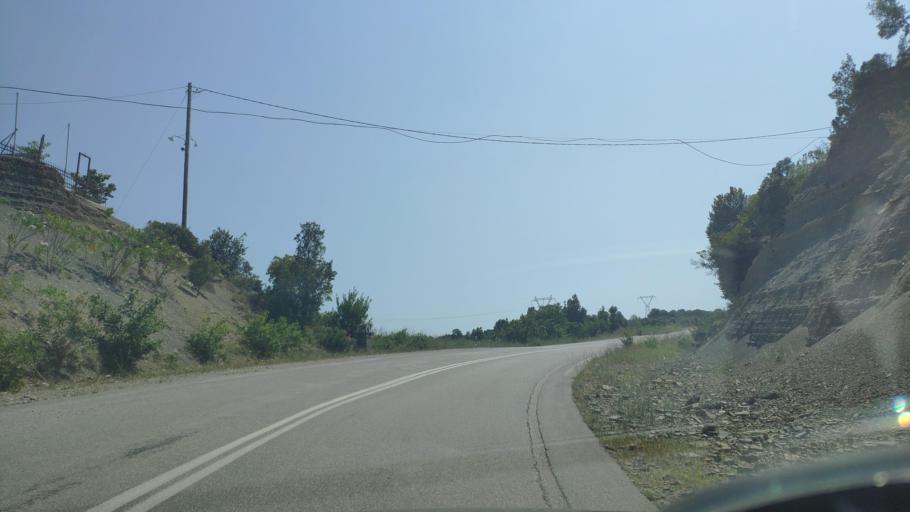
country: GR
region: Epirus
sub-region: Nomos Artas
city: Ano Kalentini
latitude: 39.2174
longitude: 21.1265
